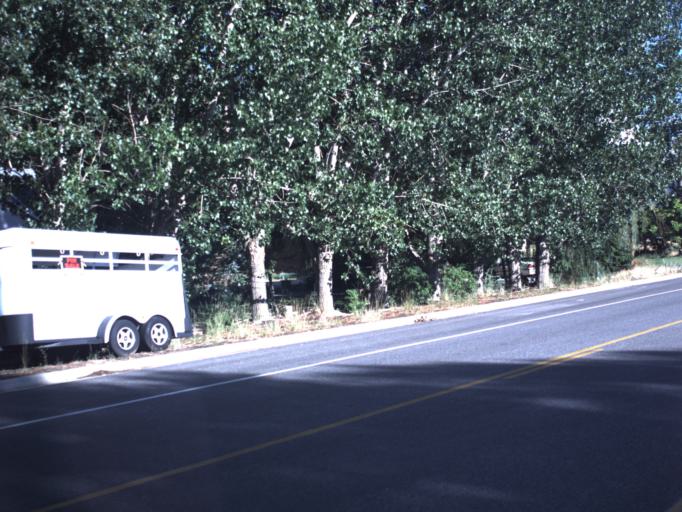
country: US
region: Utah
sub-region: Utah County
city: Mapleton
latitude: 40.1184
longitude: -111.5978
